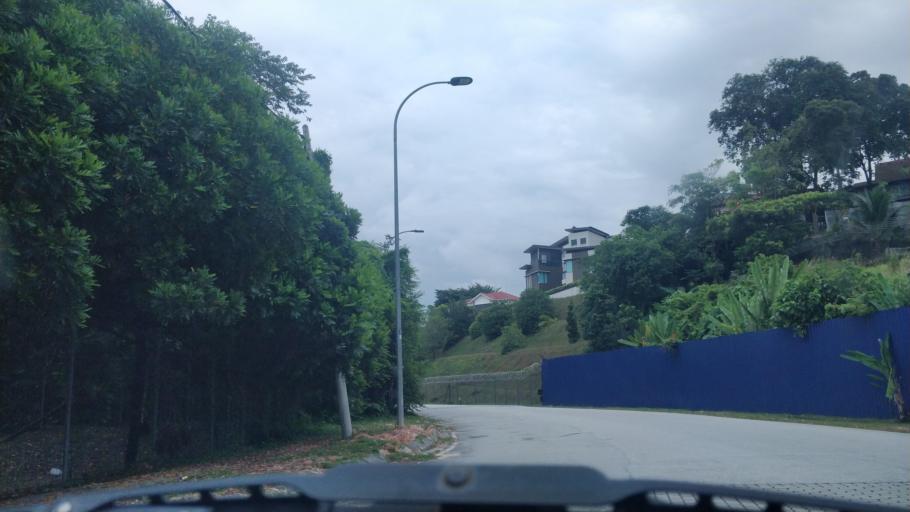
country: MY
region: Selangor
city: Kuang
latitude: 3.2057
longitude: 101.5862
